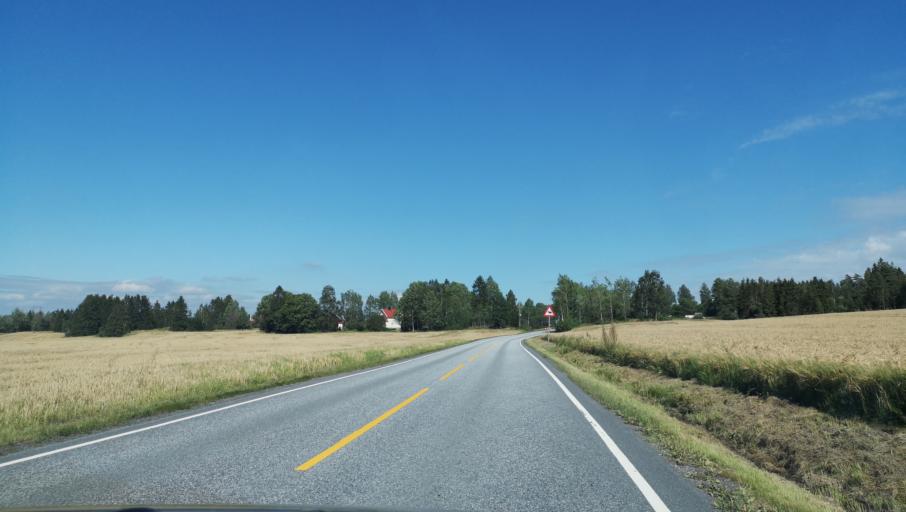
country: NO
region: Akershus
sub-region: Vestby
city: Vestby
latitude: 59.5437
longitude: 10.7865
